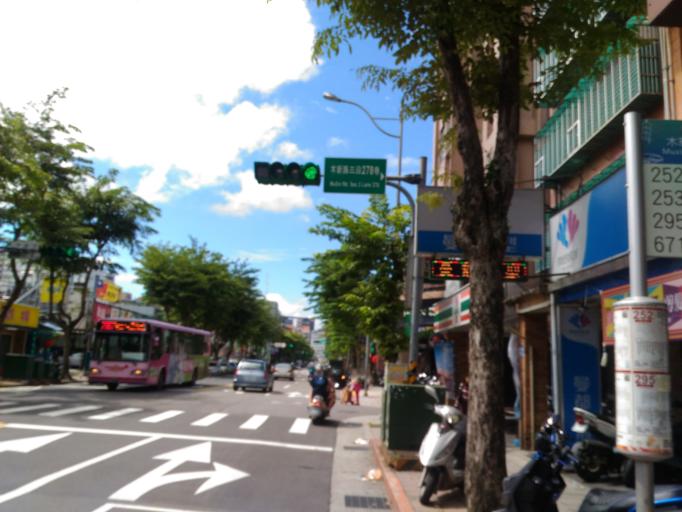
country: TW
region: Taipei
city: Taipei
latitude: 24.9812
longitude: 121.5583
